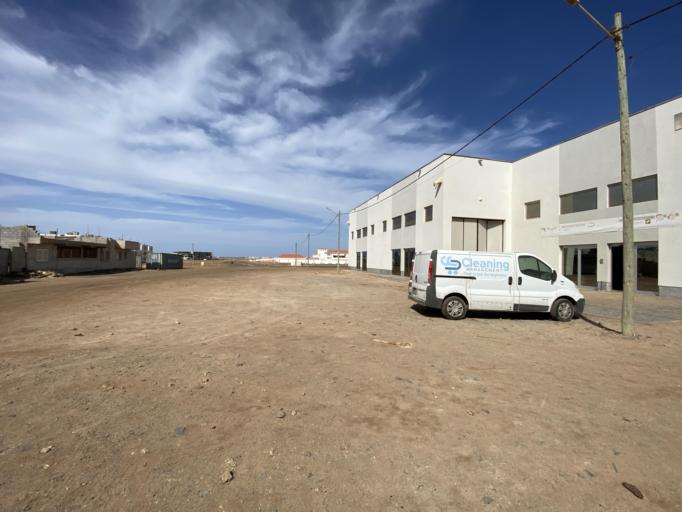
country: CV
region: Sal
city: Santa Maria
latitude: 16.6037
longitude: -22.9053
